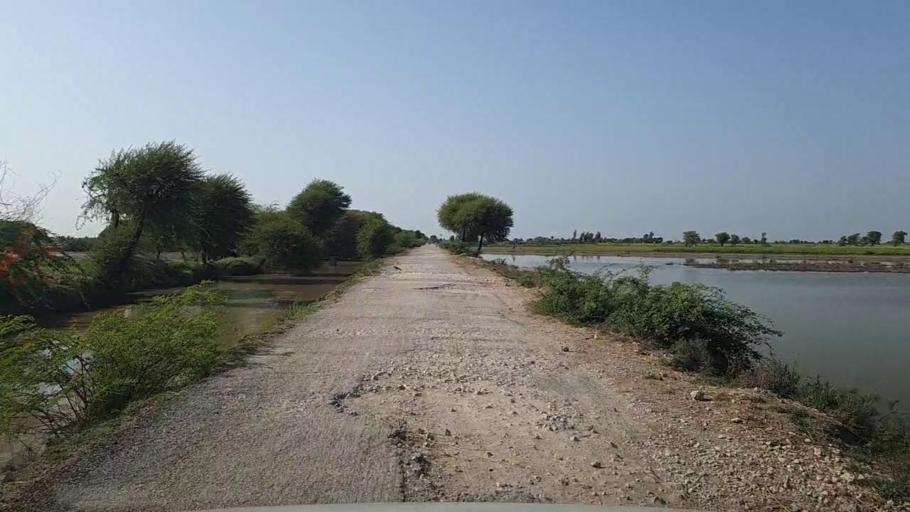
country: PK
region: Sindh
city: Kario
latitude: 24.7978
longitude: 68.5564
